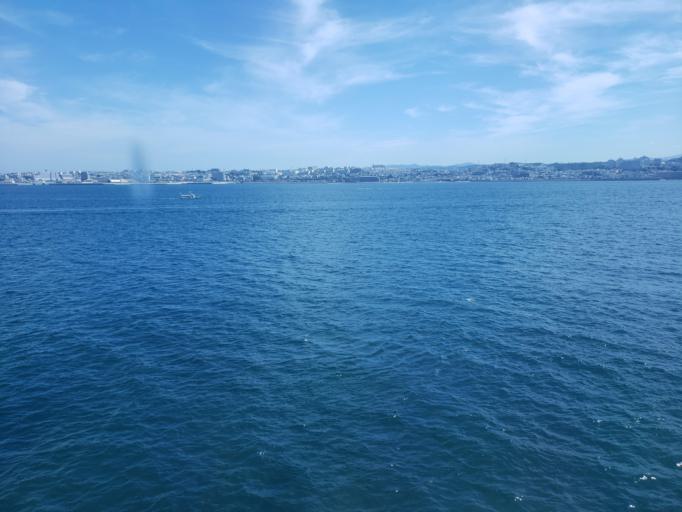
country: JP
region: Hyogo
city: Akashi
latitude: 34.6241
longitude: 135.0149
